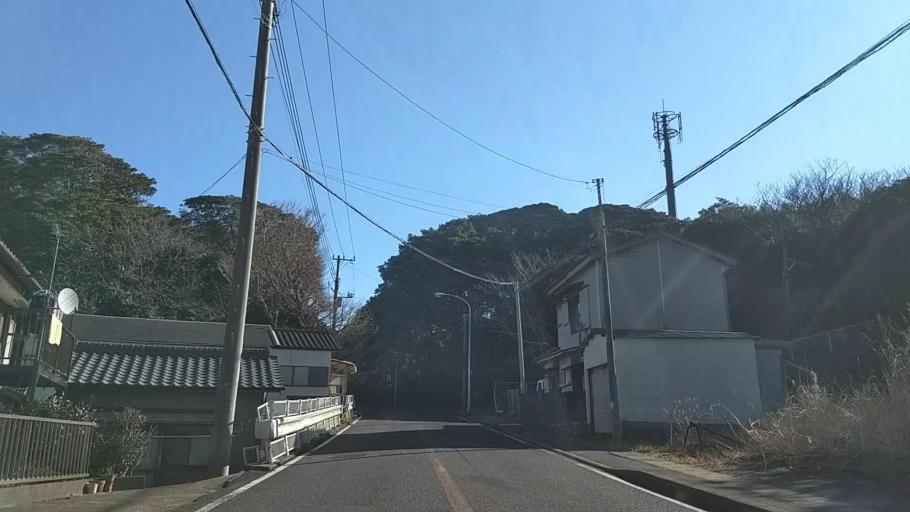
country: JP
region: Chiba
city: Hasaki
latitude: 35.7313
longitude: 140.8449
